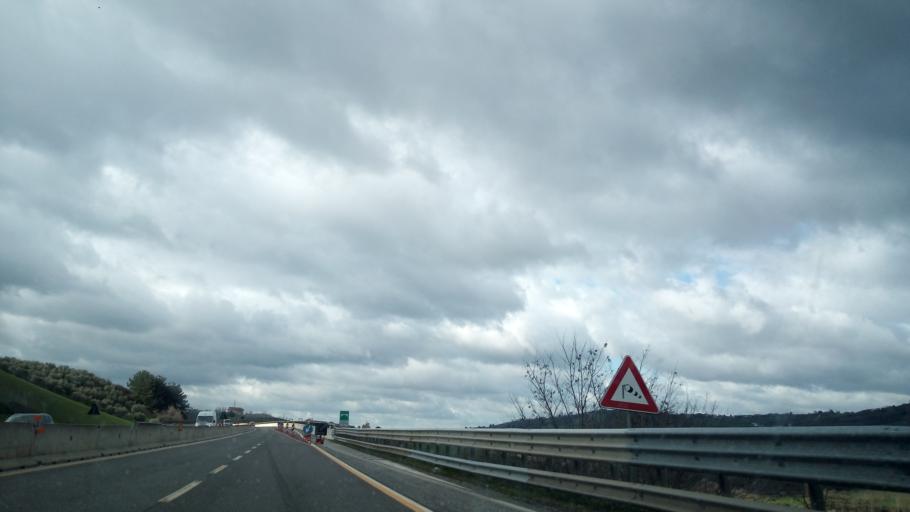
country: IT
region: Campania
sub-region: Provincia di Avellino
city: Flumeri
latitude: 41.0897
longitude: 15.1692
